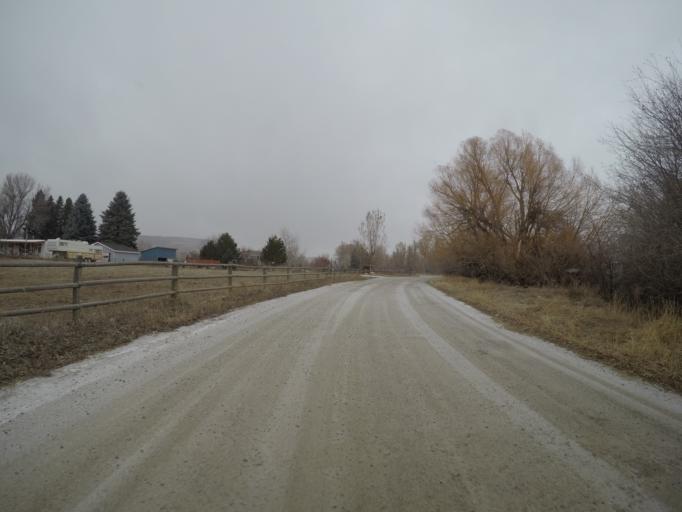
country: US
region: Montana
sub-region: Stillwater County
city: Absarokee
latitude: 45.5264
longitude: -109.4389
